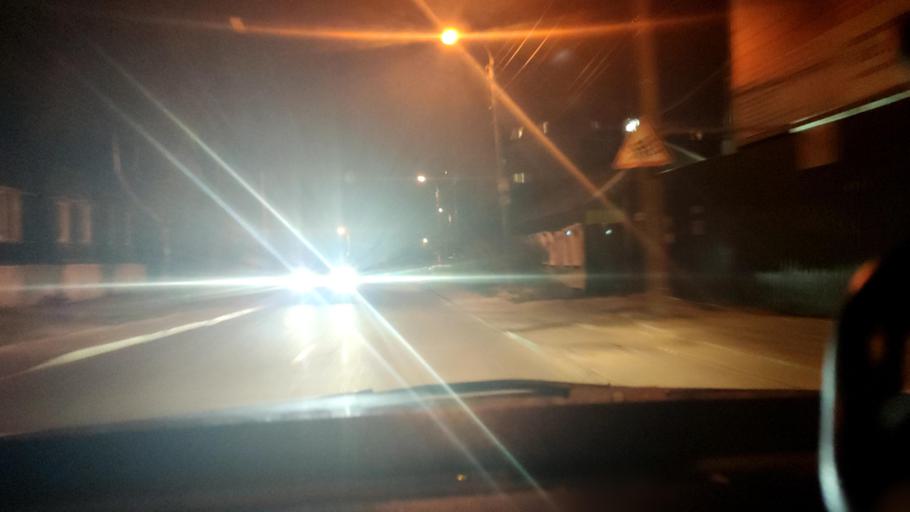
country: RU
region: Voronezj
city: Voronezh
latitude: 51.6535
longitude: 39.2015
